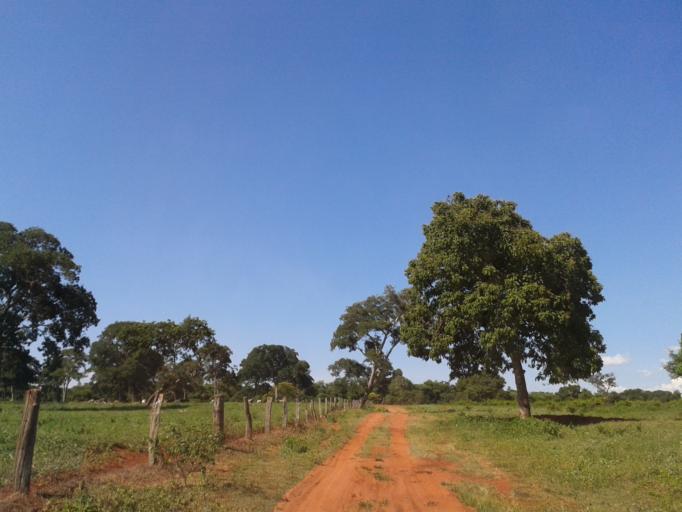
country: BR
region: Minas Gerais
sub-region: Santa Vitoria
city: Santa Vitoria
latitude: -19.1217
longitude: -50.4898
